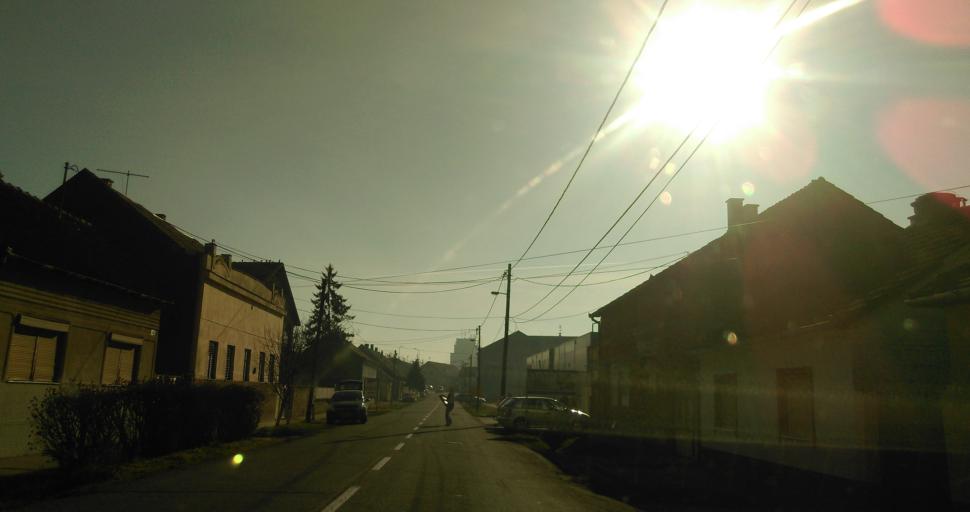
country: RS
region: Autonomna Pokrajina Vojvodina
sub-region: Sremski Okrug
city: Ruma
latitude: 45.0091
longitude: 19.8317
